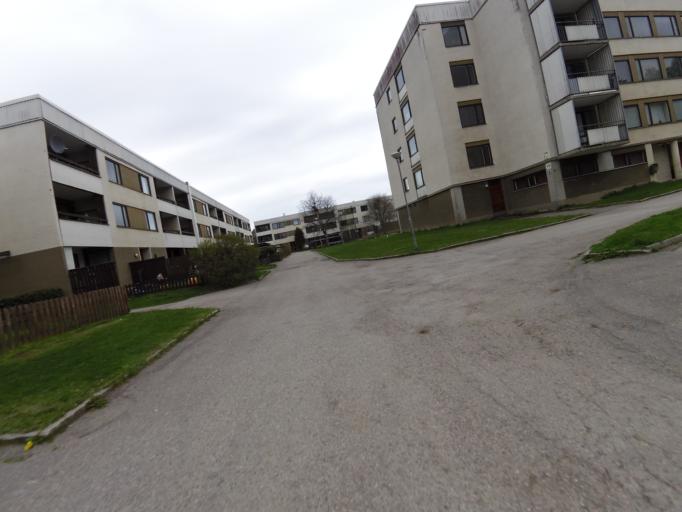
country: SE
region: Gaevleborg
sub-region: Gavle Kommun
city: Gavle
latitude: 60.6923
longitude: 17.1201
